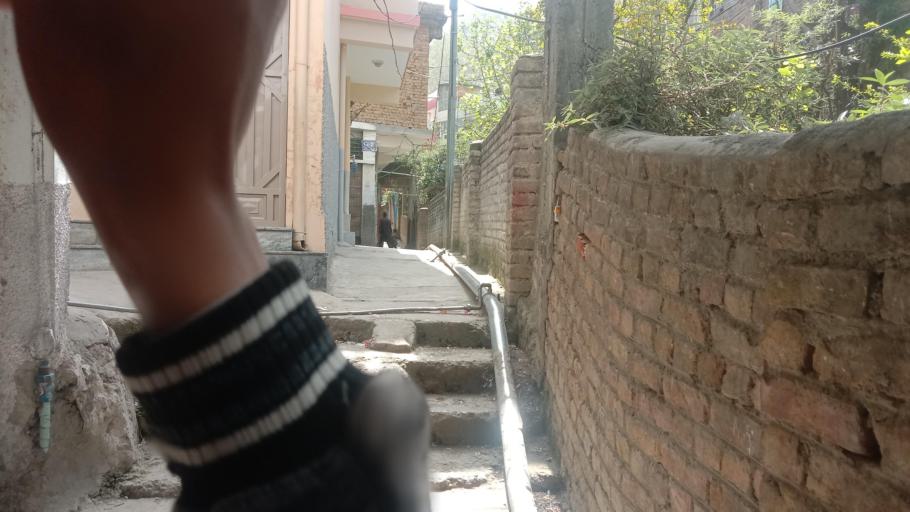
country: PK
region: Khyber Pakhtunkhwa
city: Abbottabad
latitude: 34.1301
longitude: 73.2005
